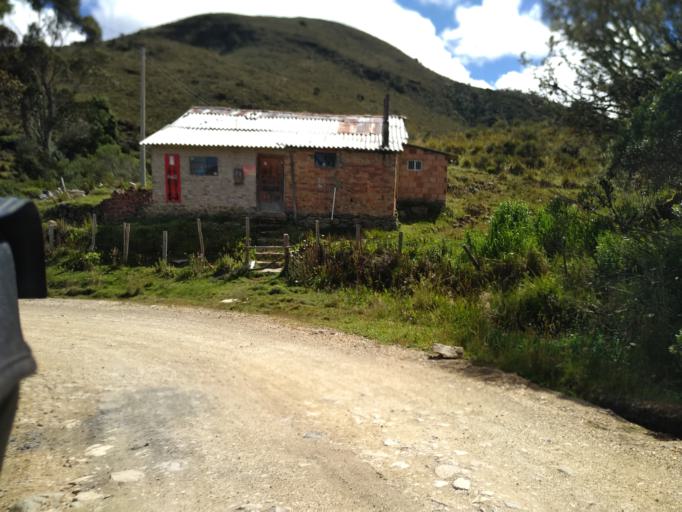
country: CO
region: Boyaca
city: Duitama
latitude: 5.9324
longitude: -73.0875
